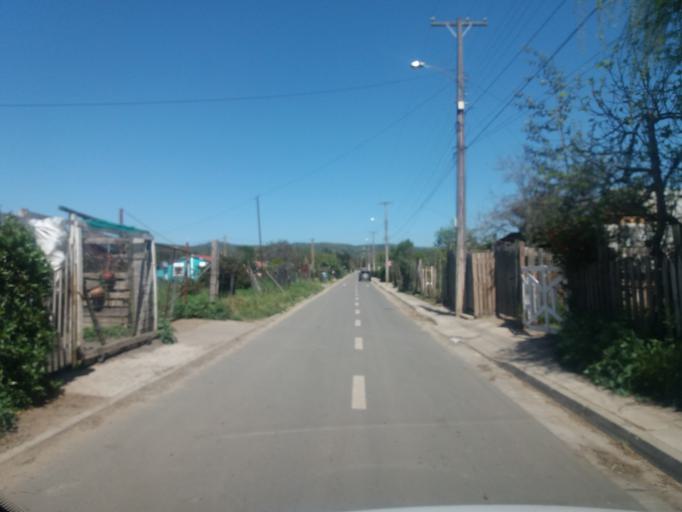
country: CL
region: Valparaiso
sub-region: Provincia de Marga Marga
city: Limache
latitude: -32.9804
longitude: -71.2893
